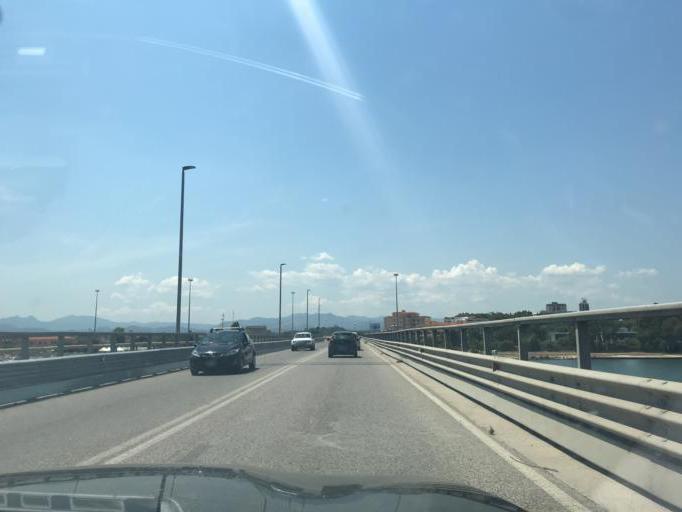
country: IT
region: Sardinia
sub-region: Provincia di Olbia-Tempio
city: Olbia
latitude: 40.9289
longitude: 9.5080
